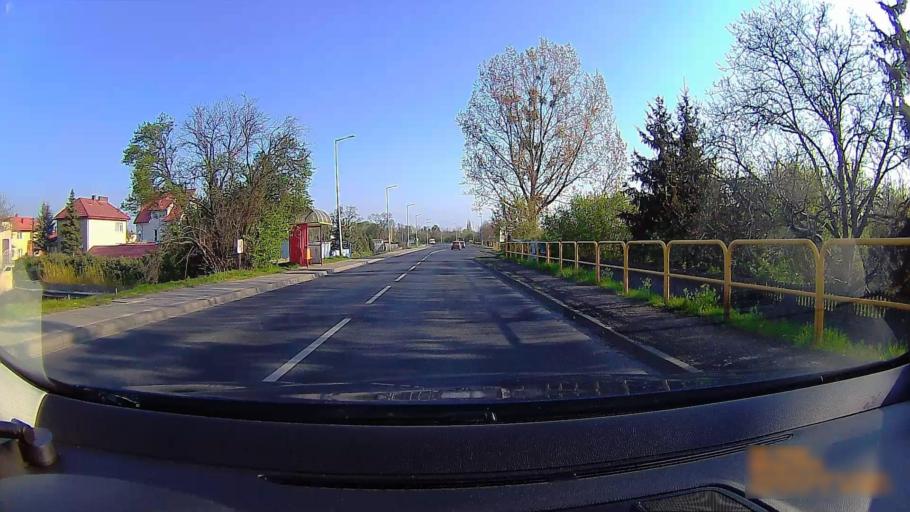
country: PL
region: Greater Poland Voivodeship
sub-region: Konin
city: Konin
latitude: 52.2051
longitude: 18.2624
